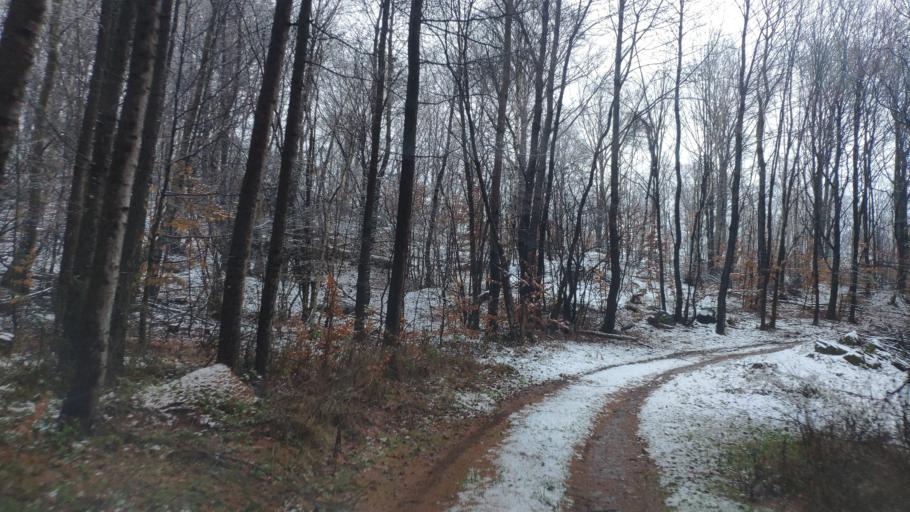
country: SK
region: Kosicky
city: Moldava nad Bodvou
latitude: 48.7378
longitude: 21.0762
